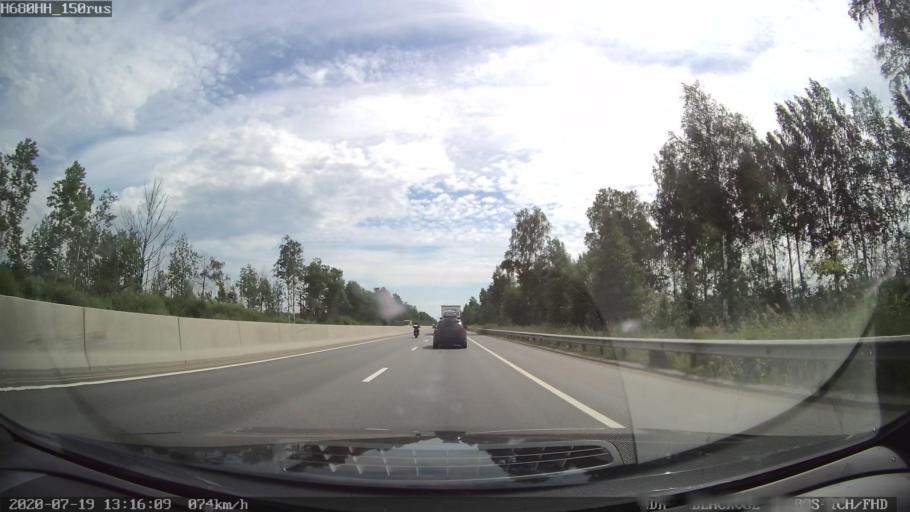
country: RU
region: St.-Petersburg
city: Kolpino
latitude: 59.7194
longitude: 30.5507
